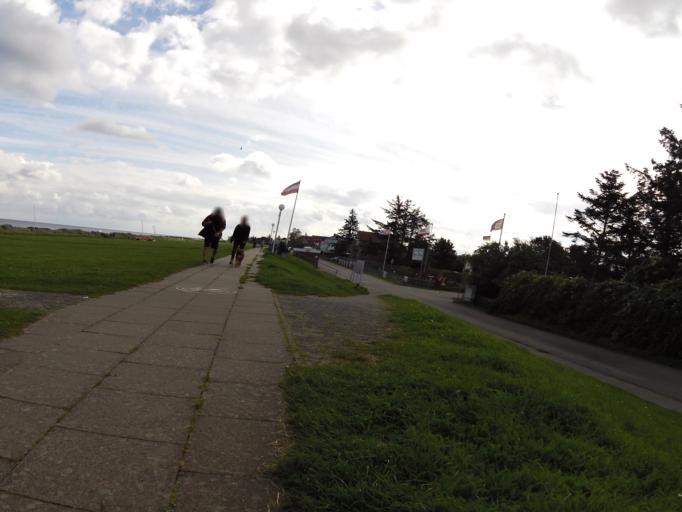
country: DE
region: Schleswig-Holstein
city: Wisch
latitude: 54.4299
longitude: 10.3616
